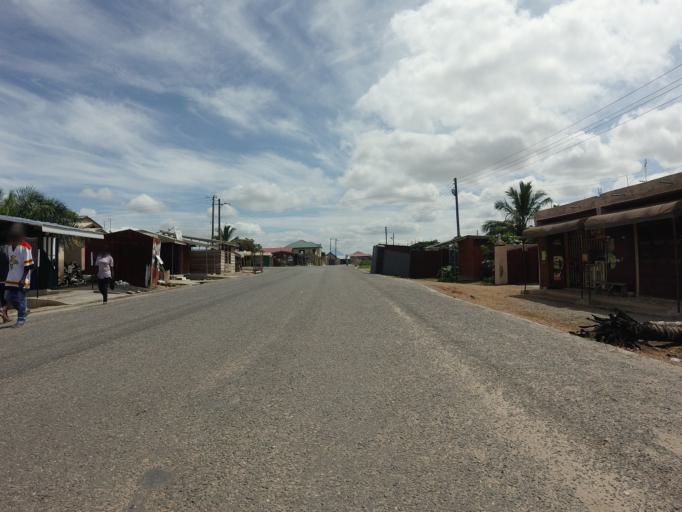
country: GH
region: Central
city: Kasoa
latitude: 5.5228
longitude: -0.4500
